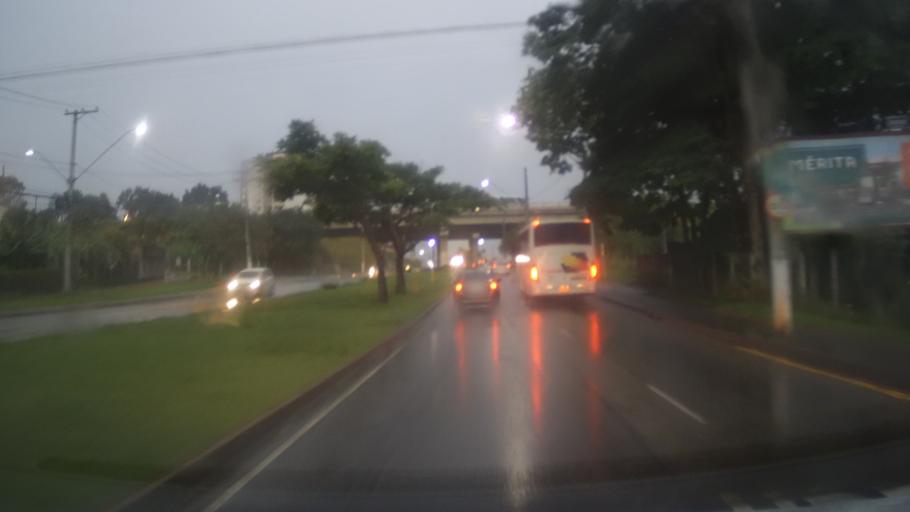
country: BR
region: Sao Paulo
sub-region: Jundiai
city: Jundiai
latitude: -23.1864
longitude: -46.9347
